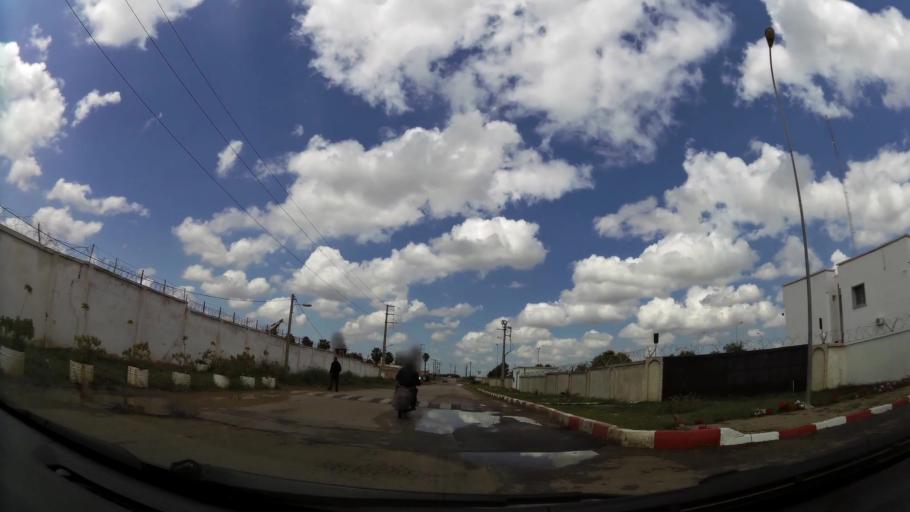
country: MA
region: Chaouia-Ouardigha
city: Nouaseur
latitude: 33.3949
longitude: -7.5786
